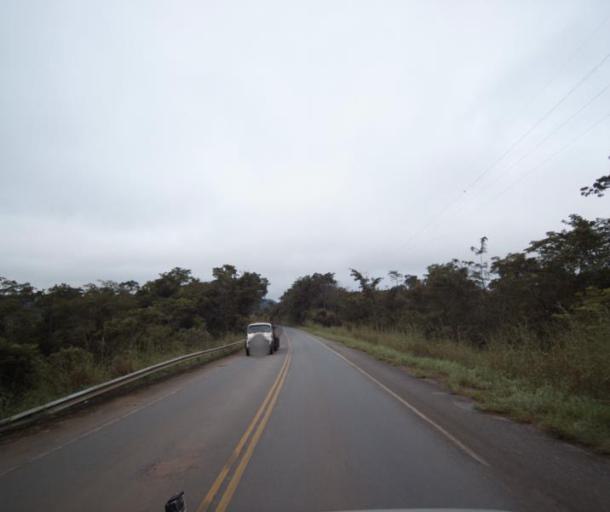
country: BR
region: Goias
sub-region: Pirenopolis
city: Pirenopolis
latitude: -15.8629
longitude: -48.7722
